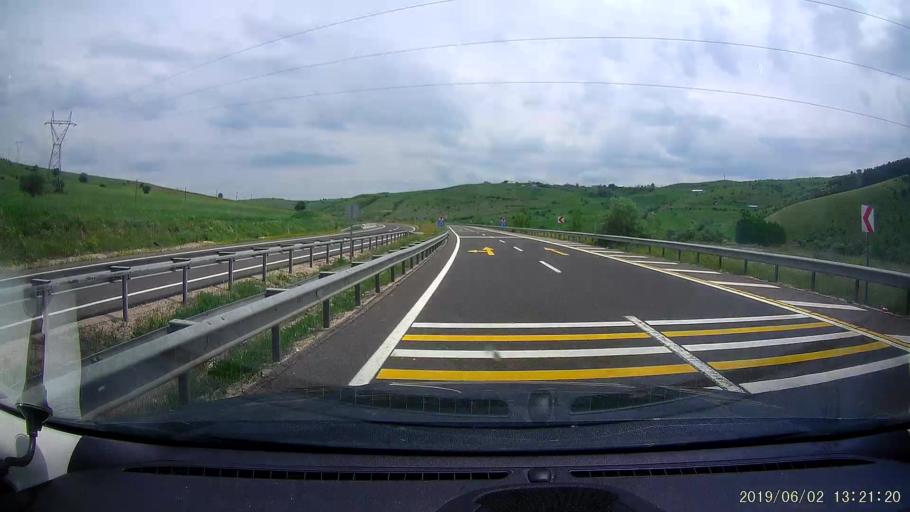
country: TR
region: Cankiri
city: Cerkes
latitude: 40.8346
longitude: 32.7731
